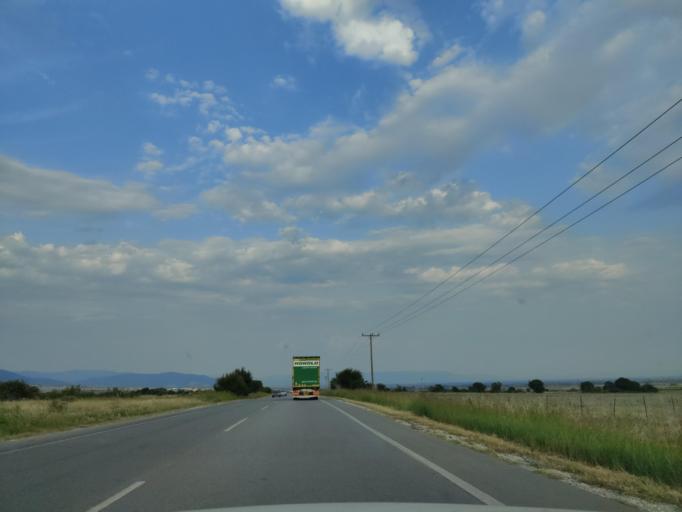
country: GR
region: East Macedonia and Thrace
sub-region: Nomos Dramas
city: Petroussa
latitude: 41.1748
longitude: 24.0148
